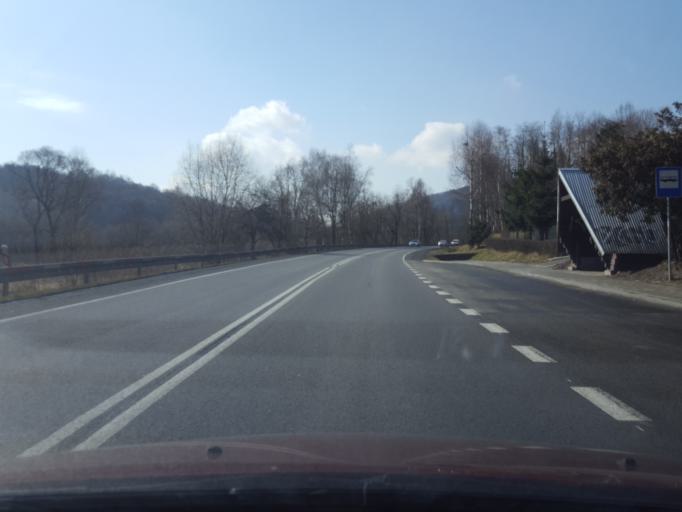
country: PL
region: Lesser Poland Voivodeship
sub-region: Powiat nowosadecki
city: Lososina Dolna
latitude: 49.7866
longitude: 20.6490
